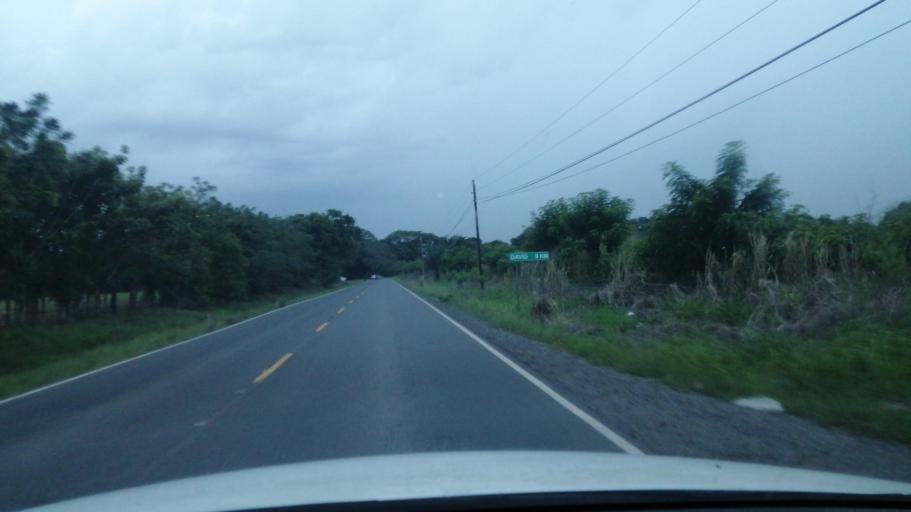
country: PA
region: Chiriqui
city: Alanje
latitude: 8.3966
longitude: -82.4879
